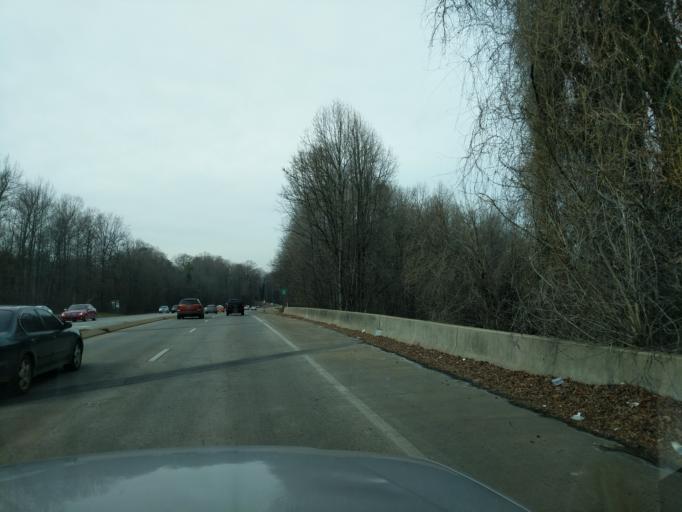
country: US
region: North Carolina
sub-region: Mecklenburg County
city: Charlotte
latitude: 35.1810
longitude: -80.8901
